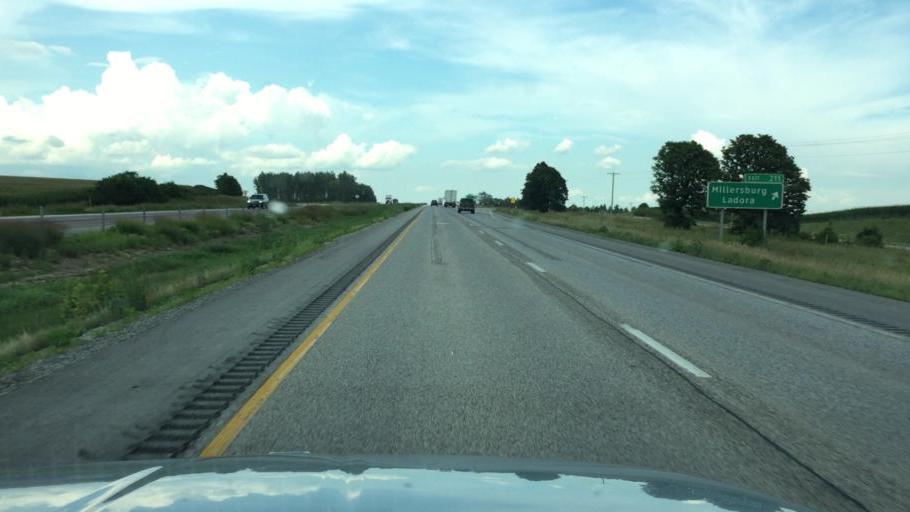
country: US
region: Iowa
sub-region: Iowa County
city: Marengo
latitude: 41.6960
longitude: -92.1698
